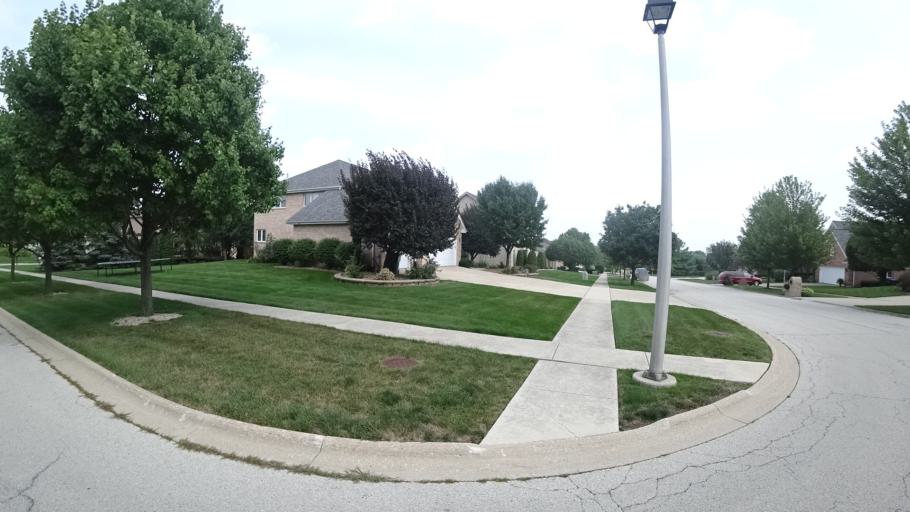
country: US
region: Illinois
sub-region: Will County
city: Goodings Grove
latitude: 41.6245
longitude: -87.9131
